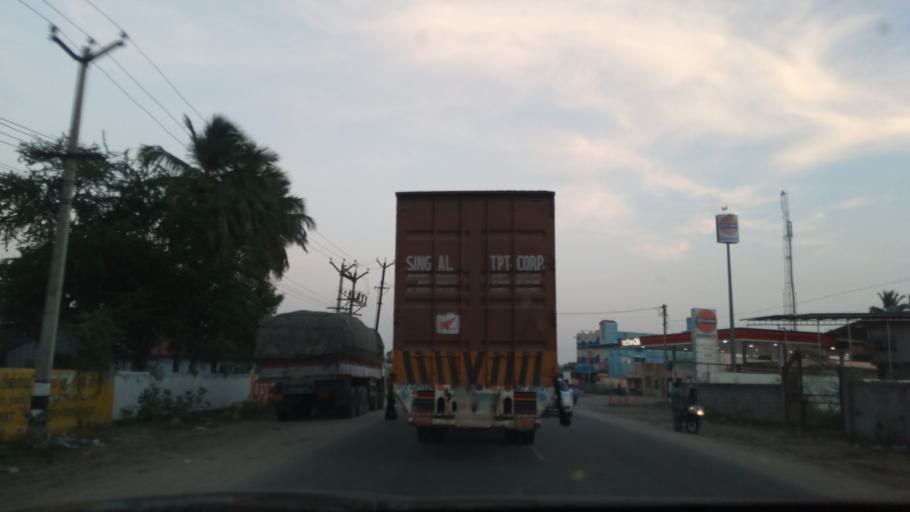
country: IN
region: Tamil Nadu
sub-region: Vellore
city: Walajapet
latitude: 12.9310
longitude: 79.3374
